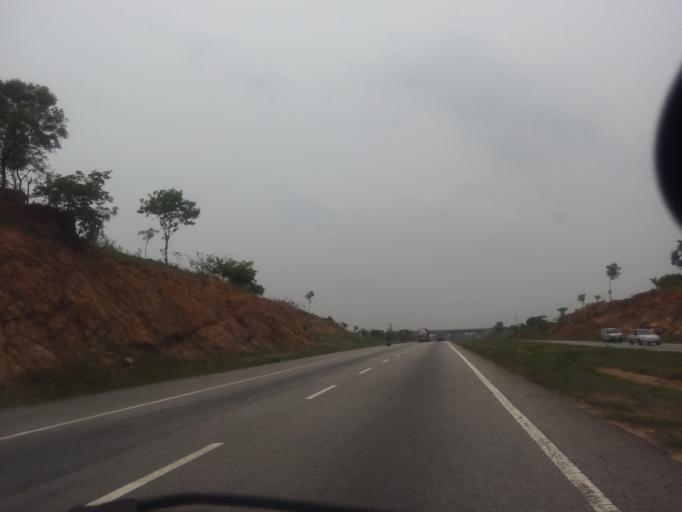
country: IN
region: Karnataka
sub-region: Bangalore Urban
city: Bangalore
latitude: 12.9678
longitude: 77.4713
